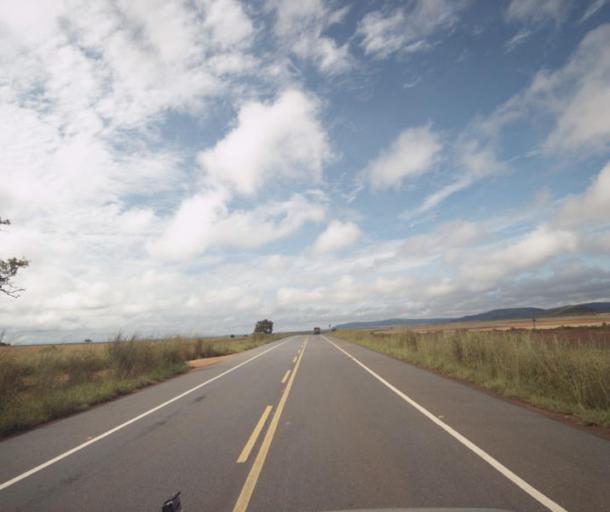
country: BR
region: Goias
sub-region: Barro Alto
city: Barro Alto
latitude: -15.2509
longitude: -48.6886
